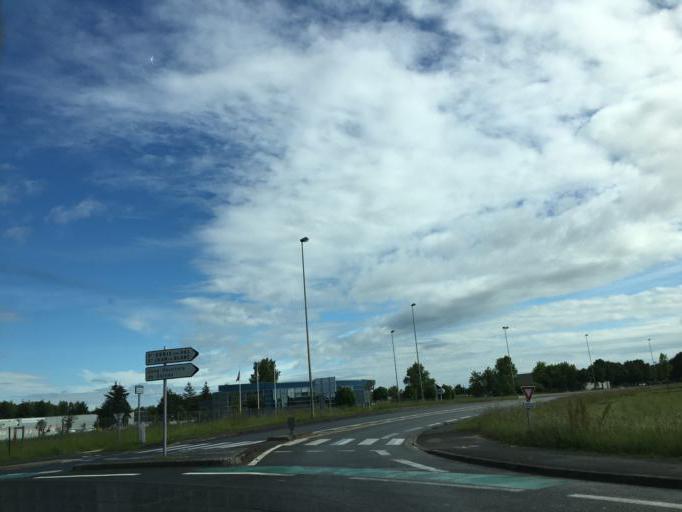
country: FR
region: Centre
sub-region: Departement du Loiret
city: Saint-Jean-le-Blanc
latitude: 47.8690
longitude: 1.9242
